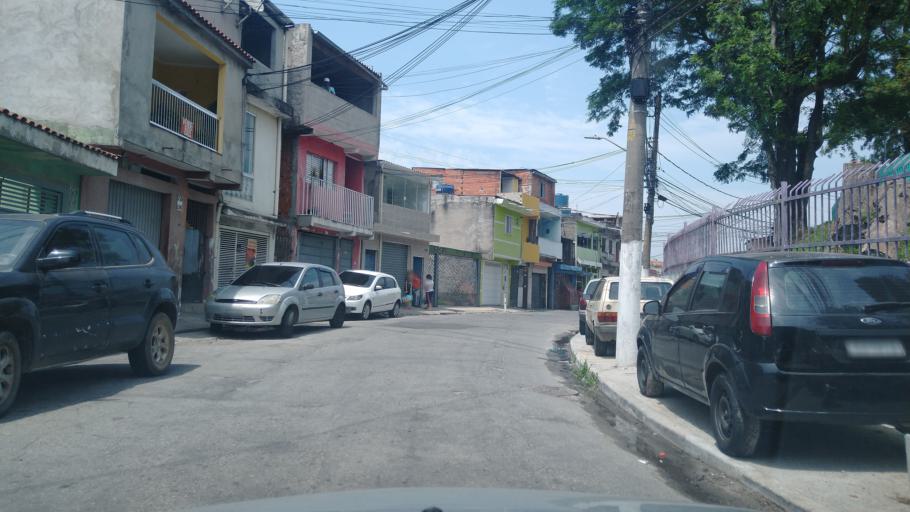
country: BR
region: Sao Paulo
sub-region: Caieiras
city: Caieiras
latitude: -23.4504
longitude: -46.6948
